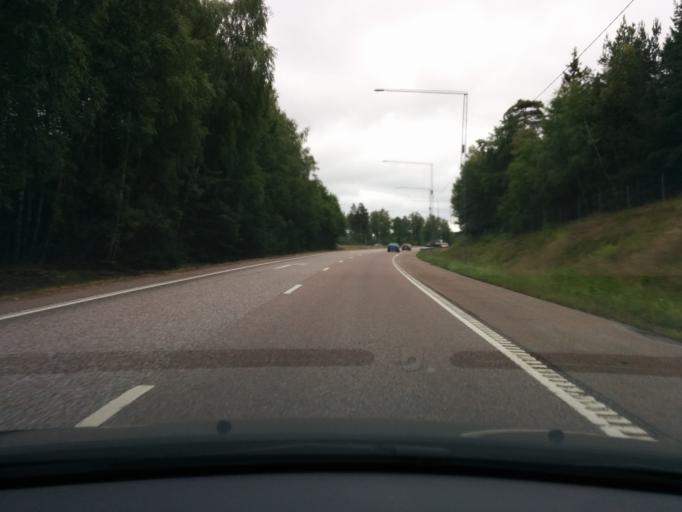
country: SE
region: Stockholm
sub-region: Sigtuna Kommun
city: Rosersberg
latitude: 59.6129
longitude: 17.8976
